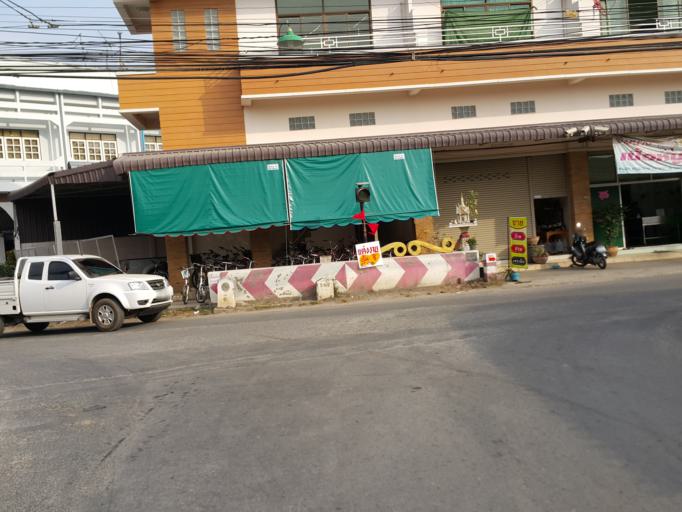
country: TH
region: Chiang Mai
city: Saraphi
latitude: 18.6793
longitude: 98.9847
